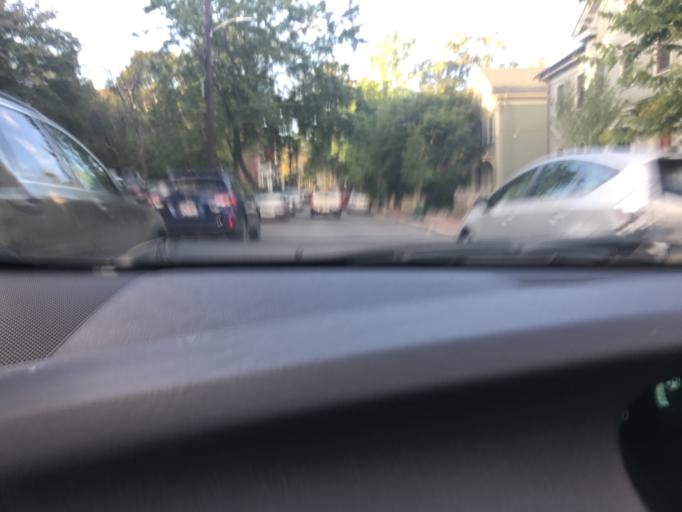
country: US
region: Massachusetts
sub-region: Middlesex County
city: Cambridge
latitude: 42.3734
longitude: -71.1070
